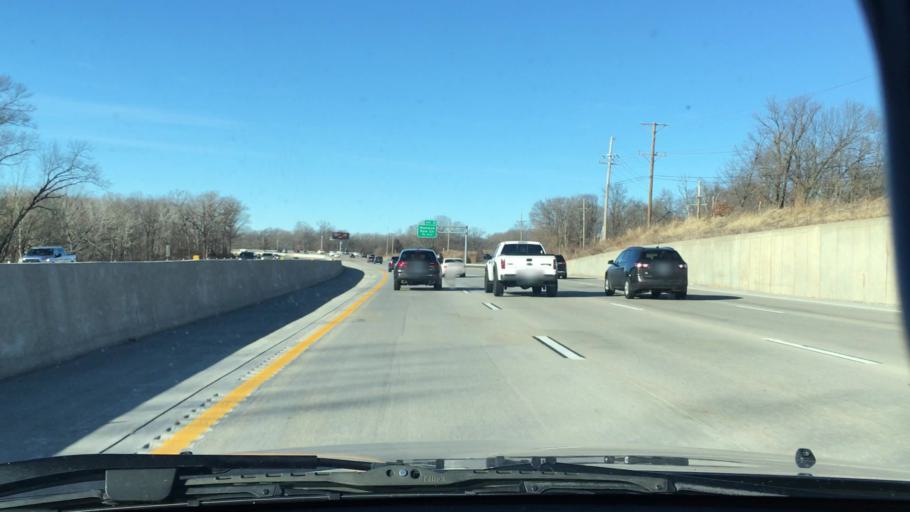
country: US
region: Missouri
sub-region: Saint Charles County
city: Weldon Spring
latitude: 38.6945
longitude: -90.6655
